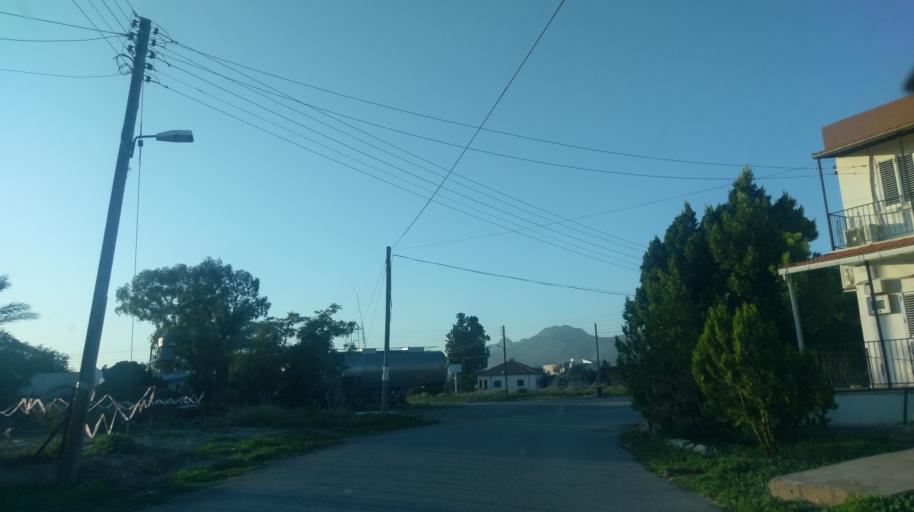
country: CY
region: Lefkosia
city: Nicosia
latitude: 35.2370
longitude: 33.5004
